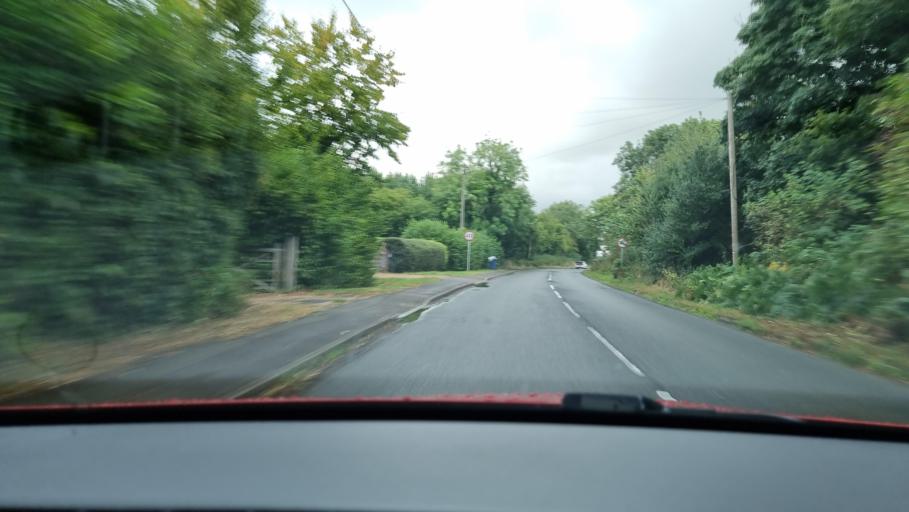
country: GB
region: England
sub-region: Buckinghamshire
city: Chesham
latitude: 51.7154
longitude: -0.5906
